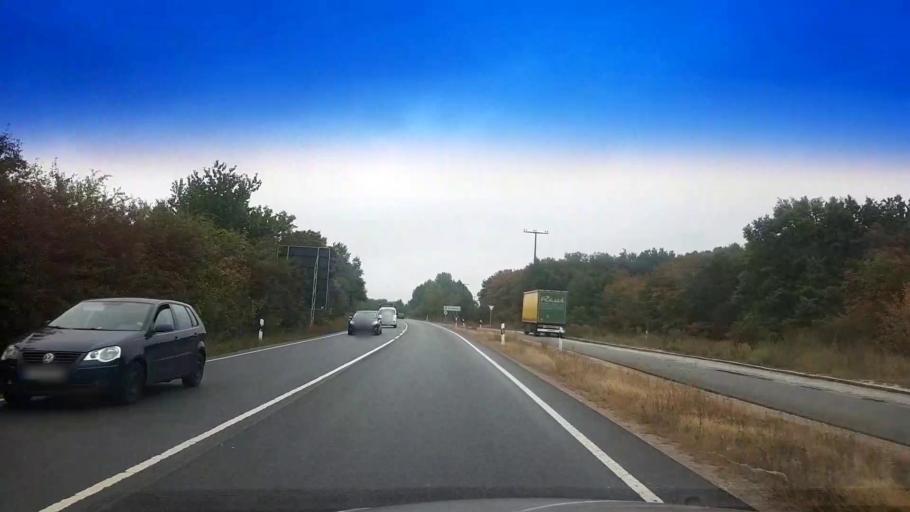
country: DE
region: Bavaria
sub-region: Upper Franconia
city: Eggolsheim
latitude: 49.7485
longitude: 11.0547
